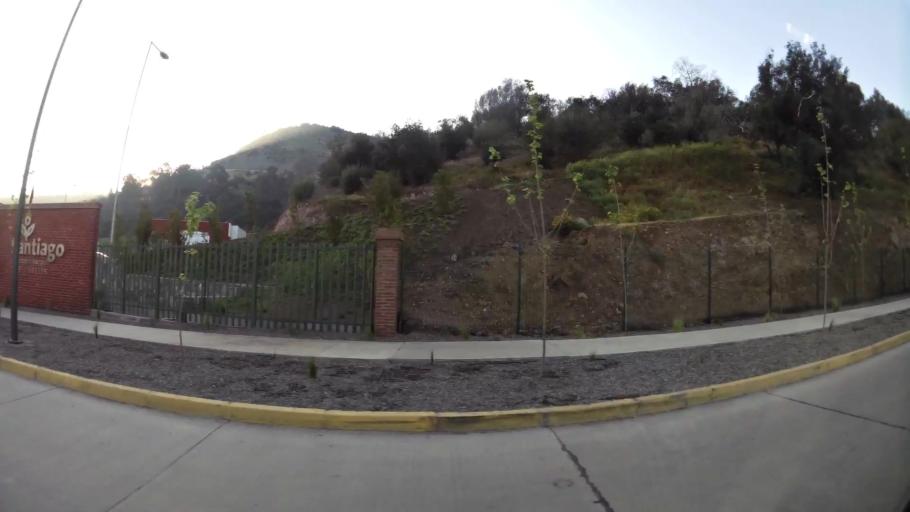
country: CL
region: Santiago Metropolitan
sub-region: Provincia de Santiago
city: Santiago
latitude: -33.3913
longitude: -70.6115
